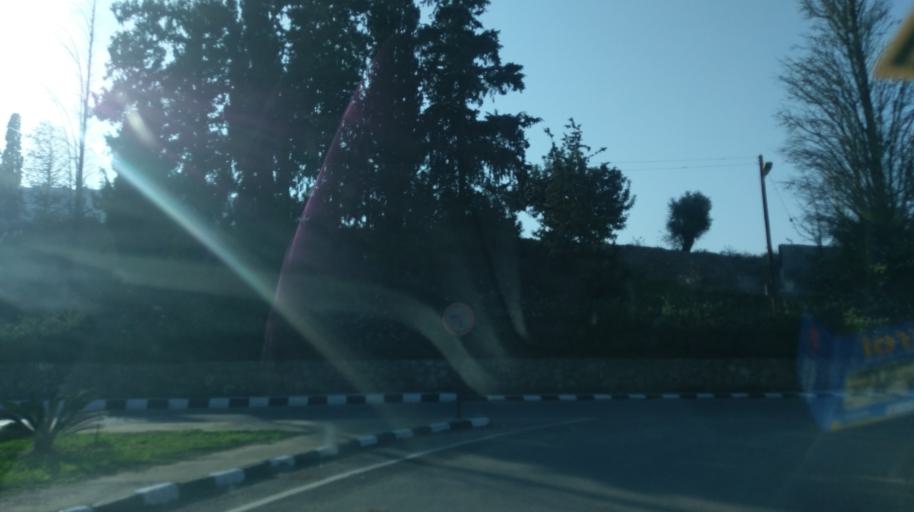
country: CY
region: Lefkosia
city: Lefka
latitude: 35.1354
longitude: 32.8342
